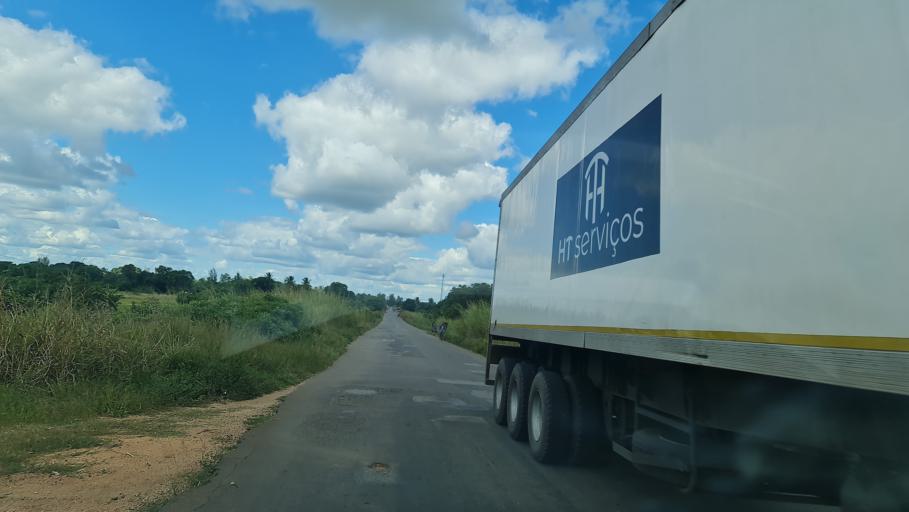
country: MZ
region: Zambezia
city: Quelimane
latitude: -17.5166
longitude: 36.2614
